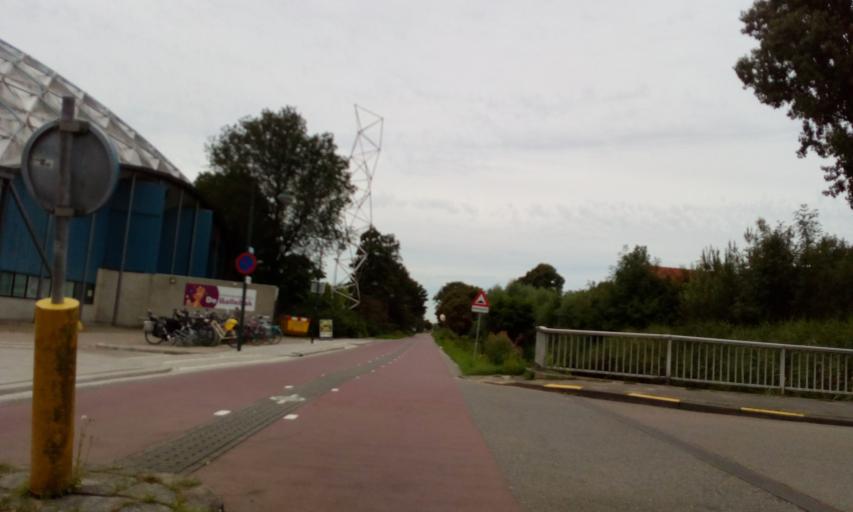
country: NL
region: South Holland
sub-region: Gemeente Zoetermeer
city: Zoetermeer
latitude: 52.0618
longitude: 4.4706
